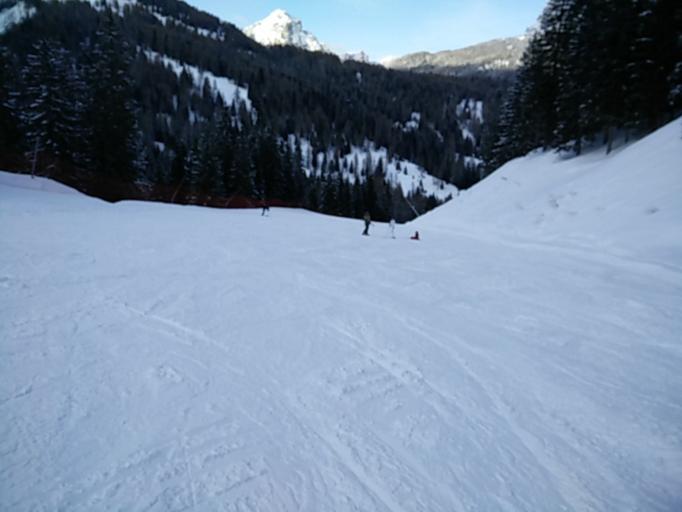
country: IT
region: Veneto
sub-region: Provincia di Belluno
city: Fusine
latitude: 46.3897
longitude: 12.0891
